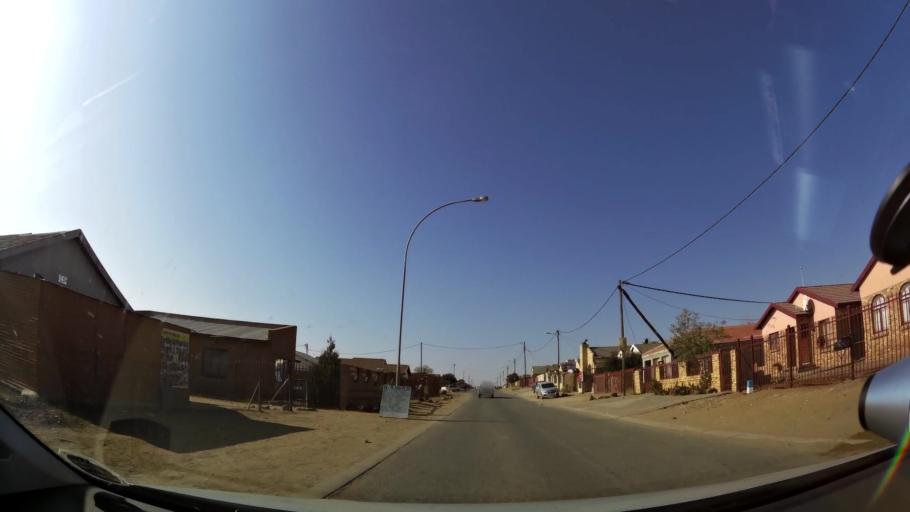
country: ZA
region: Orange Free State
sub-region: Mangaung Metropolitan Municipality
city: Bloemfontein
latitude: -29.1931
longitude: 26.2253
